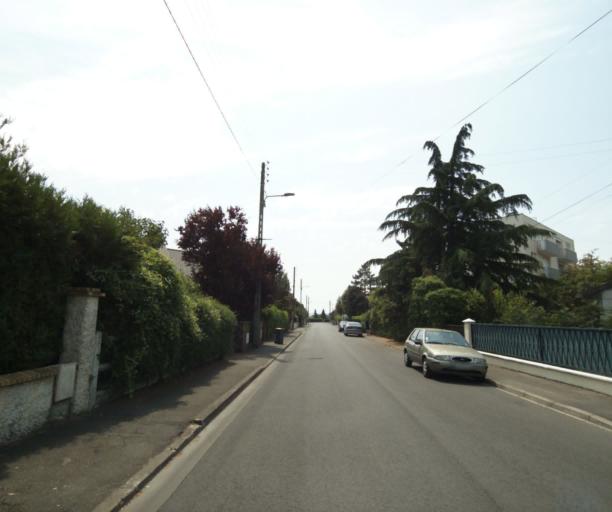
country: FR
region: Ile-de-France
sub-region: Departement des Yvelines
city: Conflans-Sainte-Honorine
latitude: 48.9944
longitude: 2.1104
